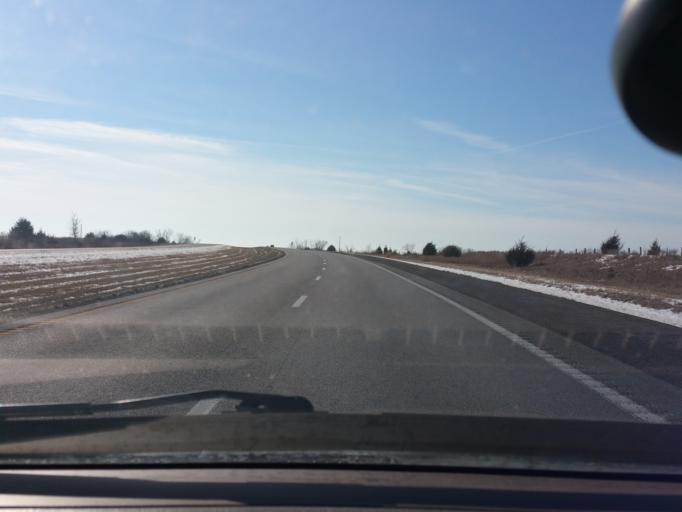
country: US
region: Missouri
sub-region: Daviess County
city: Gallatin
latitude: 39.9243
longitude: -94.1383
